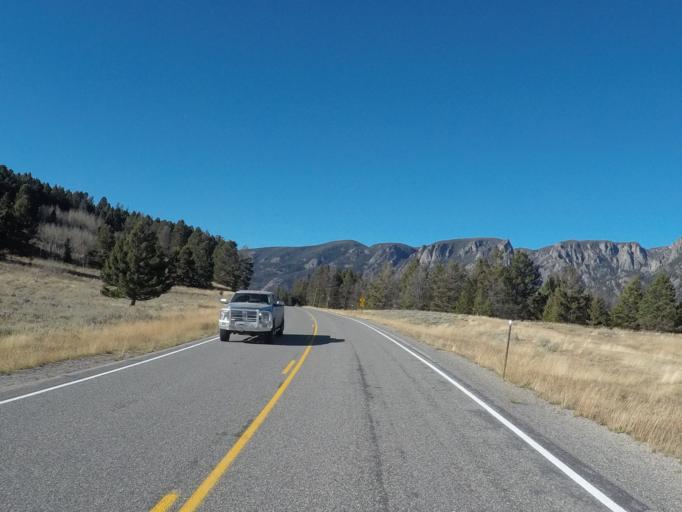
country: US
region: Montana
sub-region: Carbon County
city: Red Lodge
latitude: 44.8429
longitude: -109.4992
